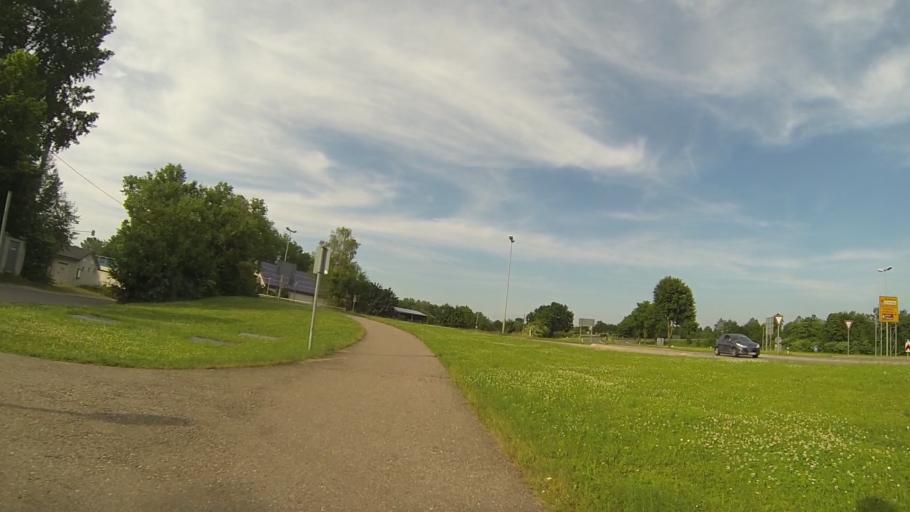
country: DE
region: Baden-Wuerttemberg
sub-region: Tuebingen Region
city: Ulm
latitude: 48.3597
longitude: 9.9633
